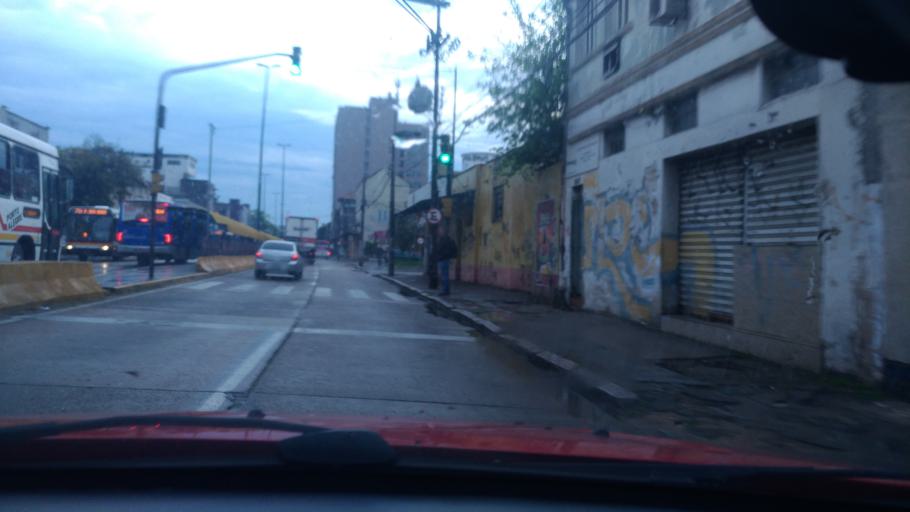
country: BR
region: Rio Grande do Sul
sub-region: Porto Alegre
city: Porto Alegre
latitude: -30.0125
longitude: -51.2033
